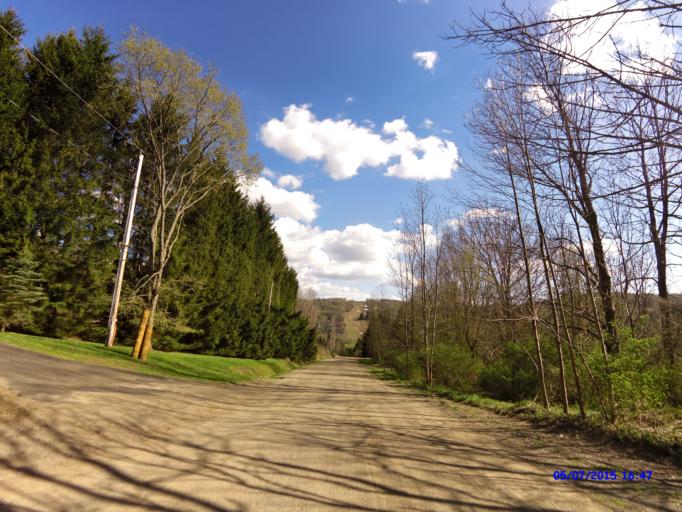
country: US
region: New York
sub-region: Cattaraugus County
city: Little Valley
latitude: 42.2808
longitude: -78.6987
